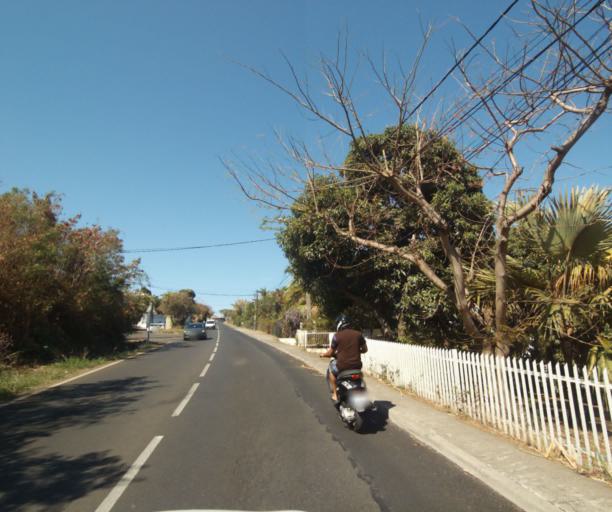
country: RE
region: Reunion
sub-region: Reunion
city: La Possession
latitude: -20.9869
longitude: 55.3321
